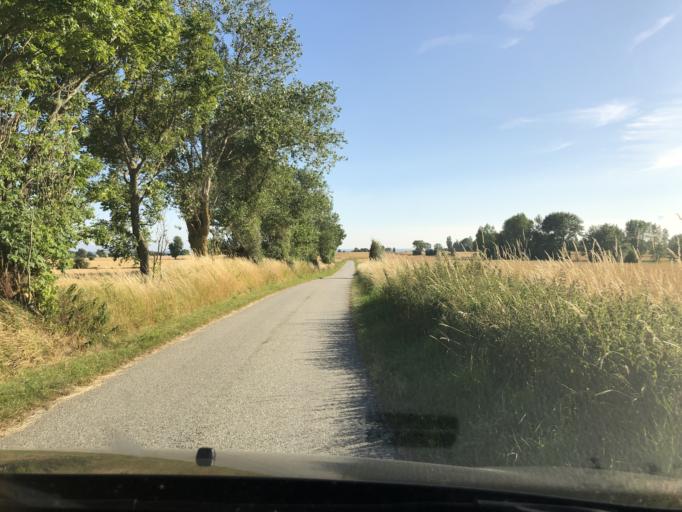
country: DK
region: South Denmark
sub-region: AEro Kommune
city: AEroskobing
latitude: 54.8563
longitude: 10.3790
